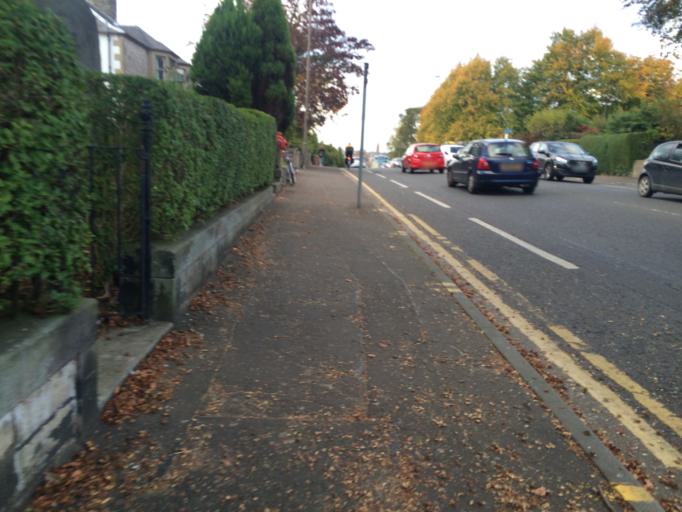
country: GB
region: Scotland
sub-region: Edinburgh
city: Edinburgh
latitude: 55.9255
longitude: -3.1733
